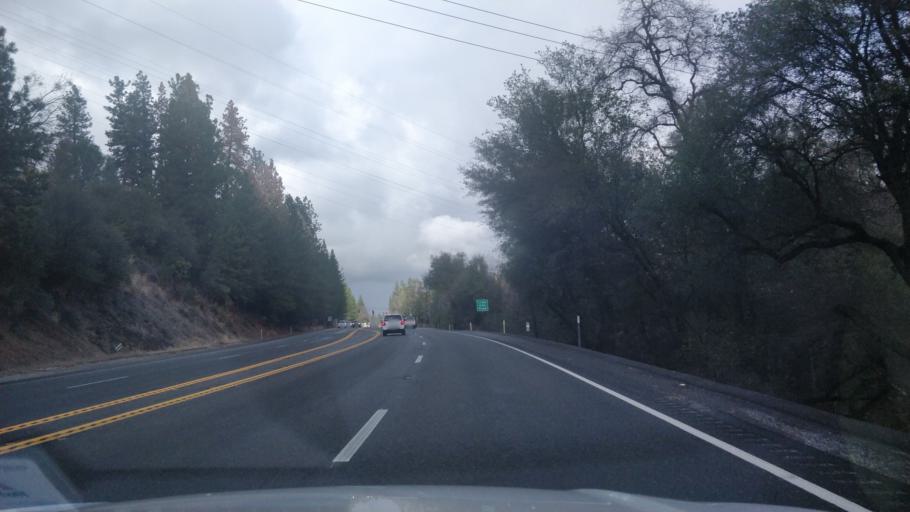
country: US
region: California
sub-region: Nevada County
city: Alta Sierra
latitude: 39.1103
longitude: -121.0835
